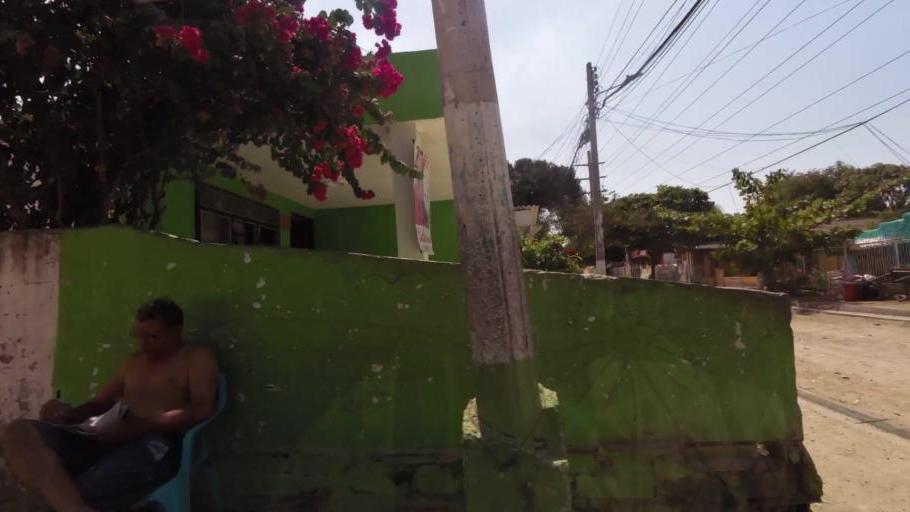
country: CO
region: Bolivar
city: Cartagena
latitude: 10.3708
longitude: -75.5070
